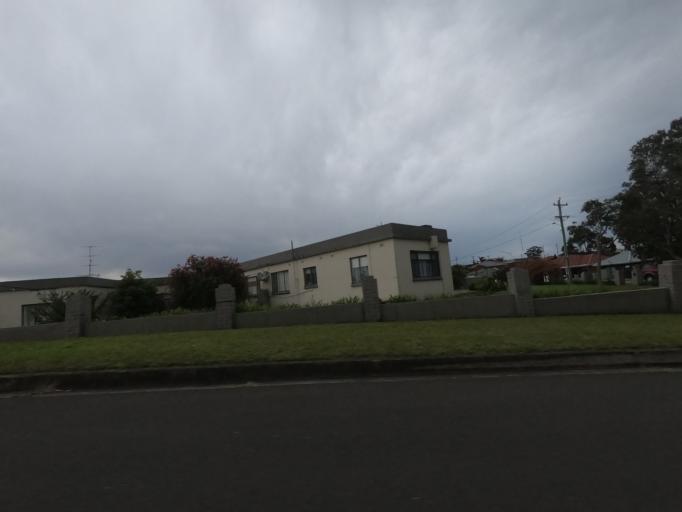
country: AU
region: New South Wales
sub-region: Wollongong
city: Lake Heights
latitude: -34.4816
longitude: 150.8638
